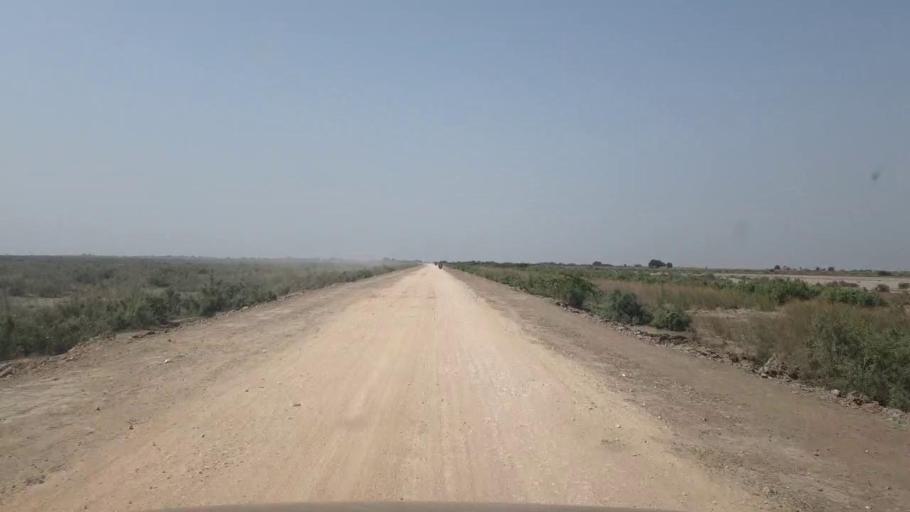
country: PK
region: Sindh
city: Jati
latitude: 24.3752
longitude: 68.5722
